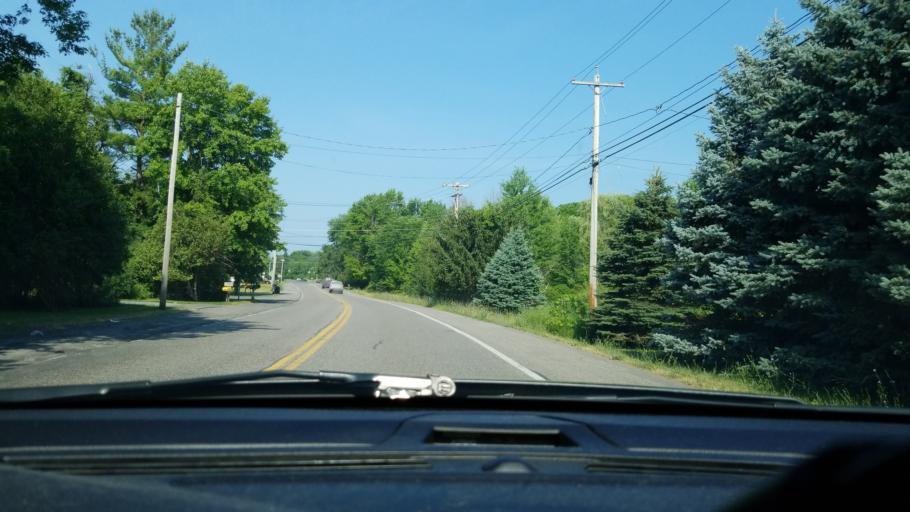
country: US
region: New York
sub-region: Onondaga County
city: North Syracuse
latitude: 43.1278
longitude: -76.0746
